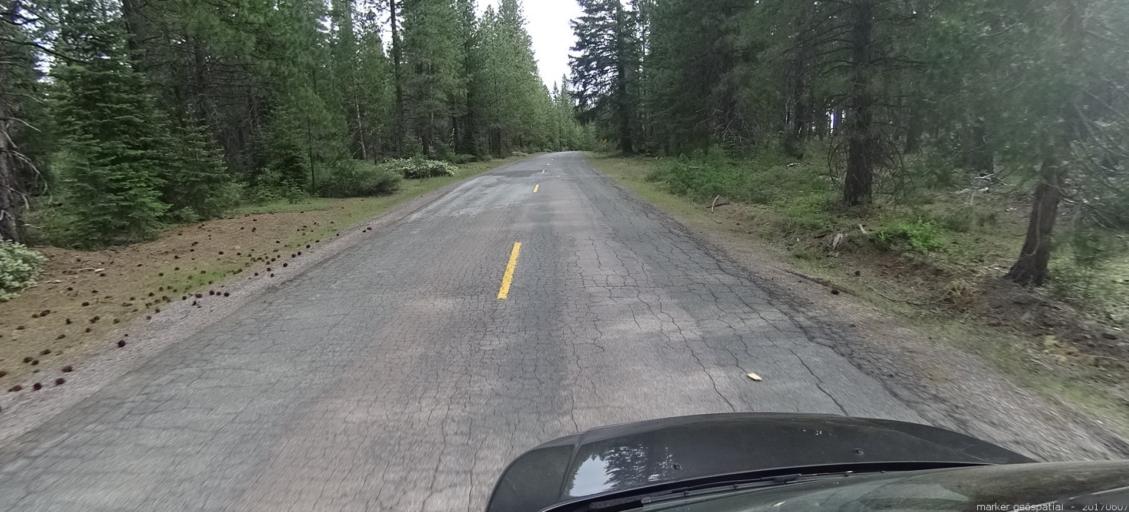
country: US
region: California
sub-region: Shasta County
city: Burney
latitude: 41.1839
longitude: -121.7073
